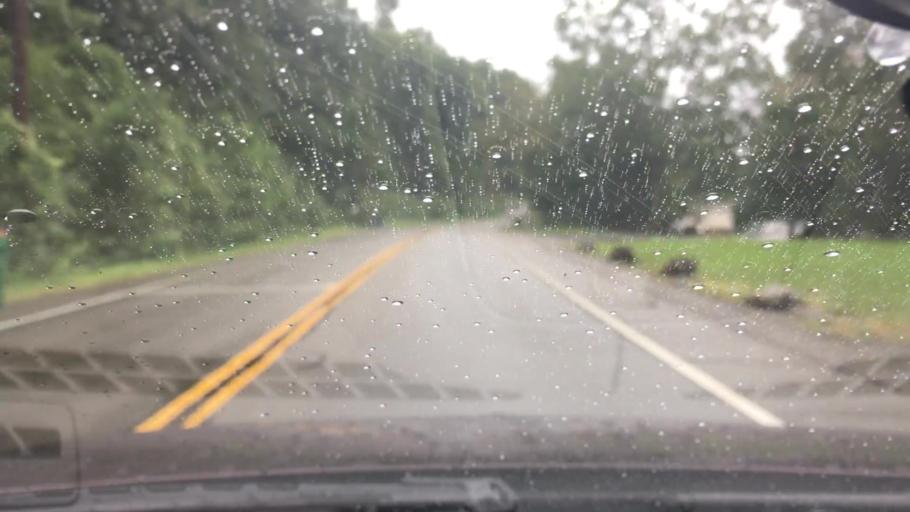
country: US
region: New York
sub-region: Dutchess County
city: Hillside Lake
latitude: 41.5690
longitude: -73.8216
